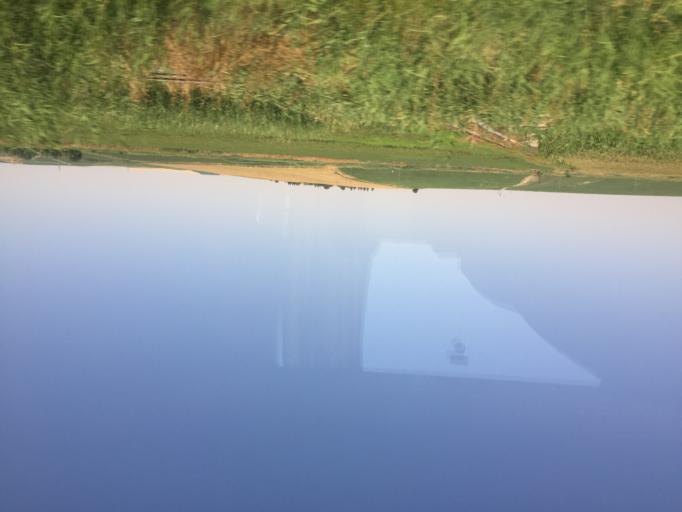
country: TR
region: Diyarbakir
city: Tepe
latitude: 37.8507
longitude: 40.7485
